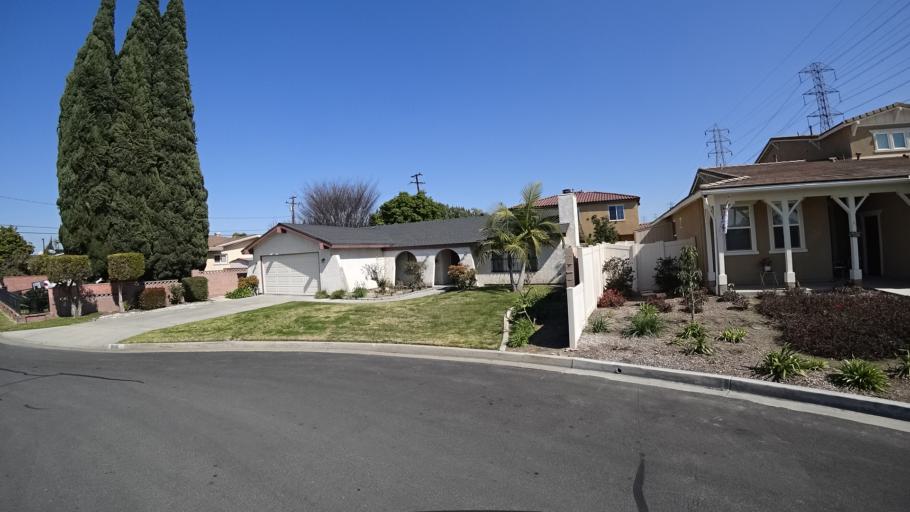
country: US
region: California
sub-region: Orange County
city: Garden Grove
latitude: 33.8076
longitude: -117.9433
